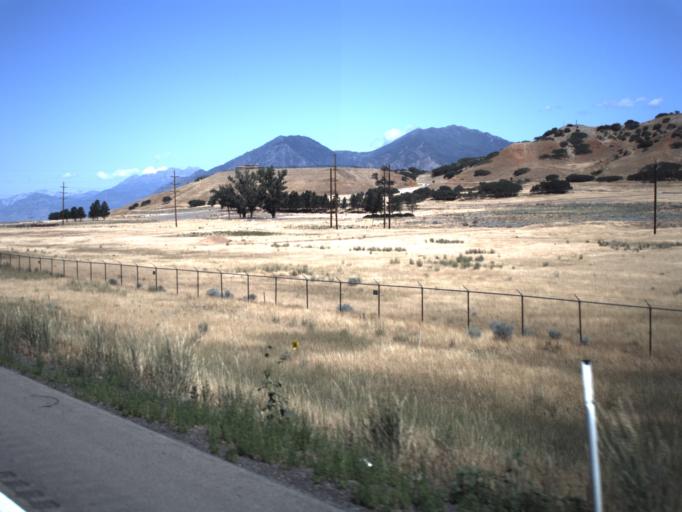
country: US
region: Utah
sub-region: Utah County
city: Mapleton
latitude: 40.0775
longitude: -111.5825
